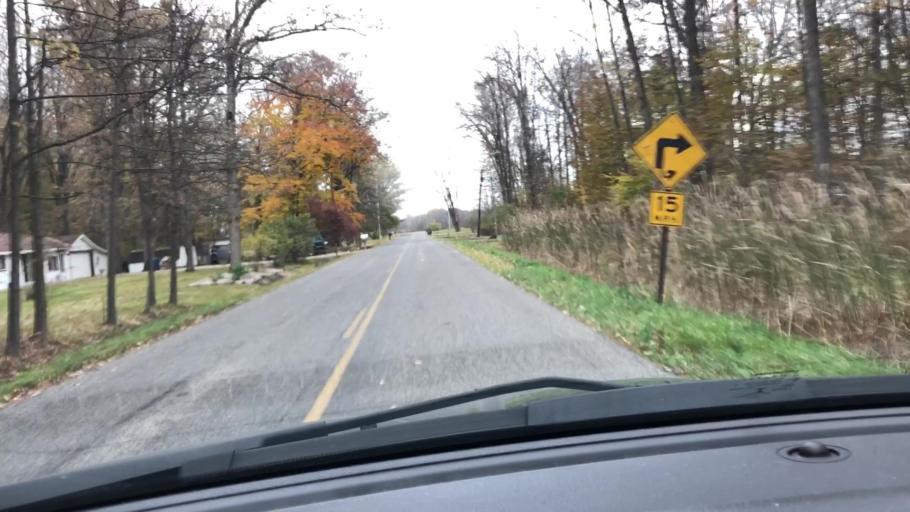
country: US
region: Michigan
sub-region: Midland County
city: Midland
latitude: 43.6413
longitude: -84.3335
